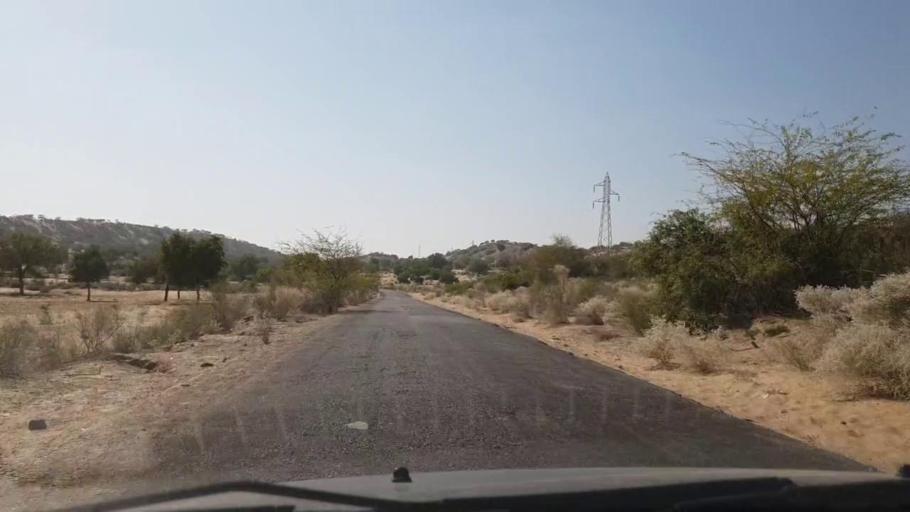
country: PK
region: Sindh
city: Mithi
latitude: 24.6814
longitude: 69.7792
